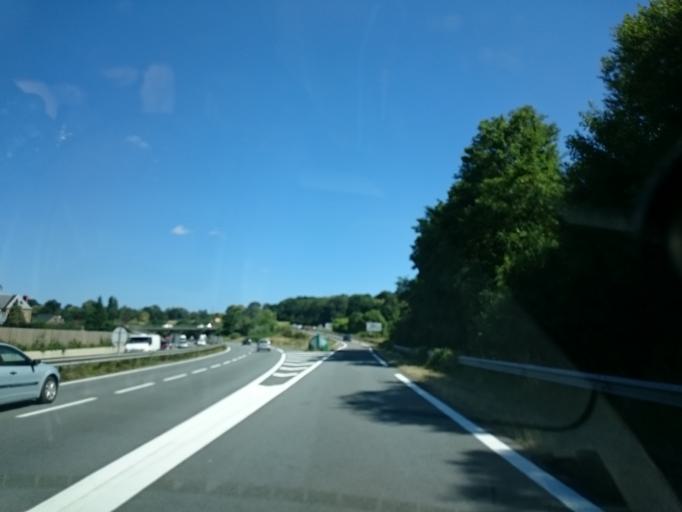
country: FR
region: Brittany
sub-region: Departement d'Ille-et-Vilaine
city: Saint-Pere
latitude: 48.5631
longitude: -1.9254
